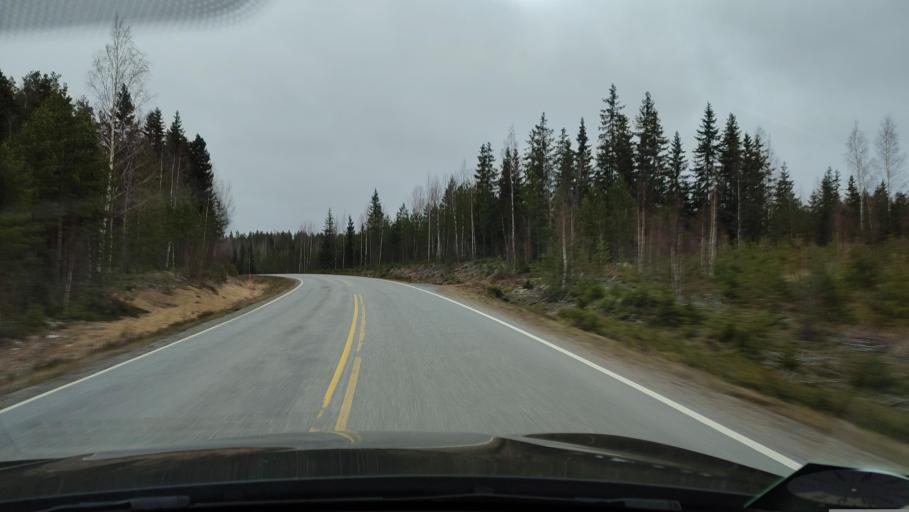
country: FI
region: Southern Ostrobothnia
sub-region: Suupohja
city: Karijoki
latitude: 62.2374
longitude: 21.7576
